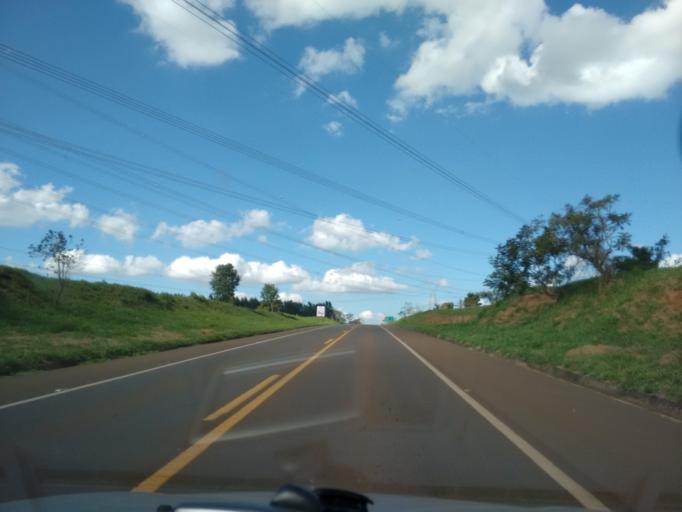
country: BR
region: Sao Paulo
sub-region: Sao Carlos
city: Sao Carlos
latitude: -22.0640
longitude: -47.9352
